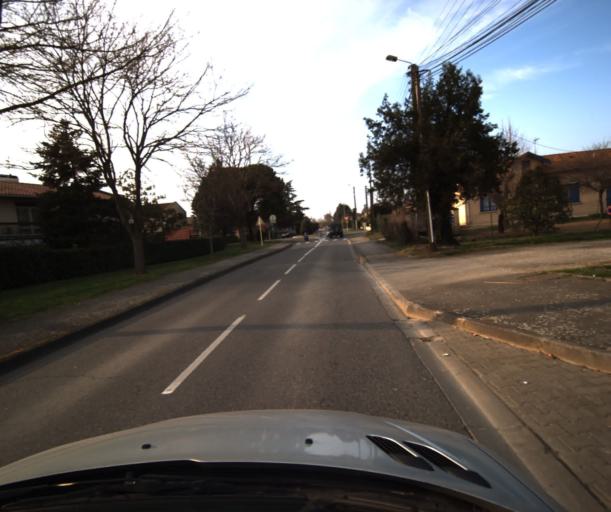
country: FR
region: Midi-Pyrenees
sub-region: Departement de la Haute-Garonne
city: Launaguet
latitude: 43.6791
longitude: 1.4540
